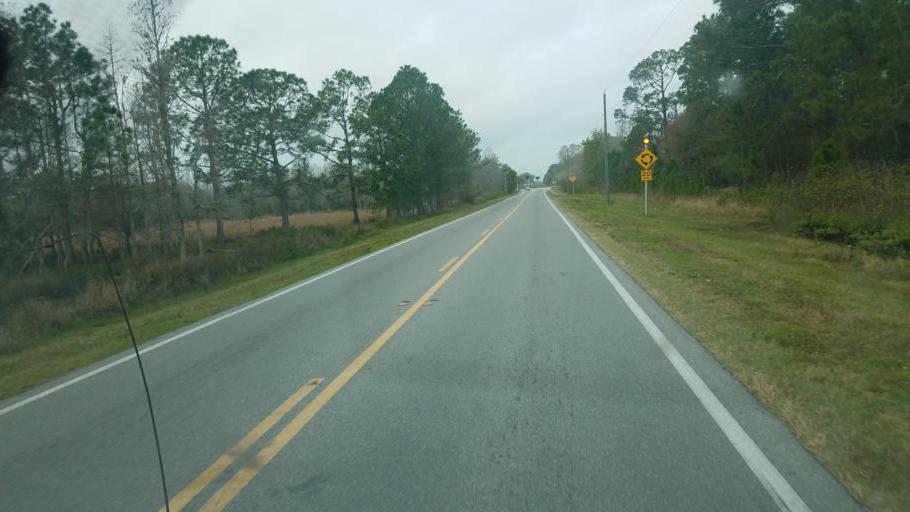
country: US
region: Florida
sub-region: Polk County
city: Polk City
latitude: 28.2585
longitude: -81.8205
